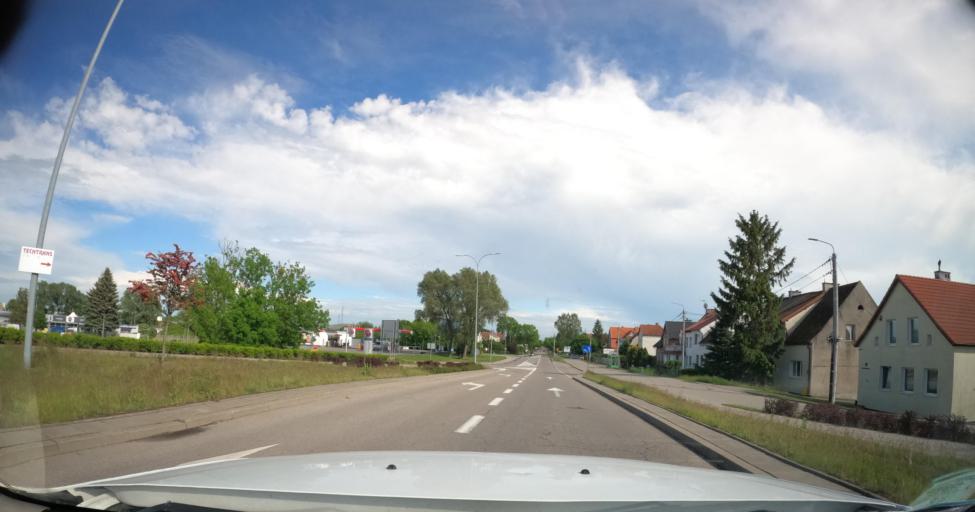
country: PL
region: Warmian-Masurian Voivodeship
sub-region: Powiat elblaski
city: Elblag
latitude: 54.1661
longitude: 19.3758
